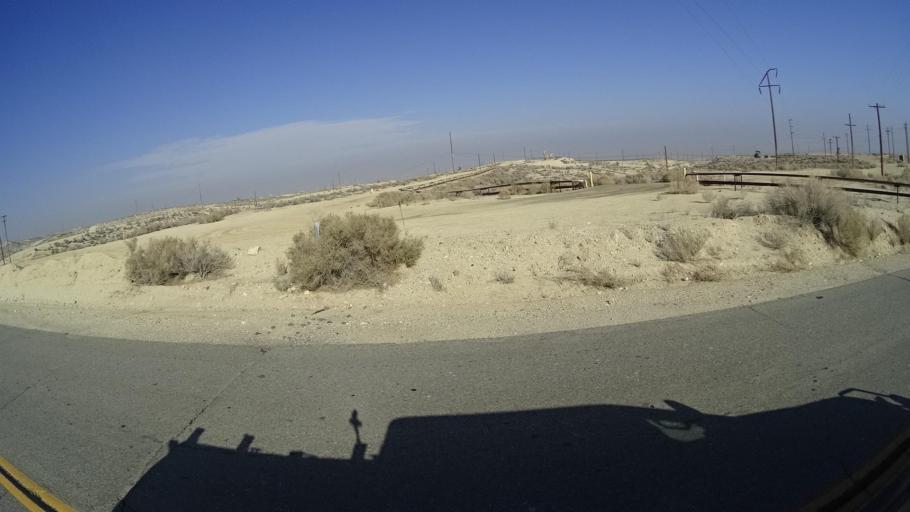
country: US
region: California
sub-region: Kern County
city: Taft Heights
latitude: 35.1441
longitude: -119.5107
